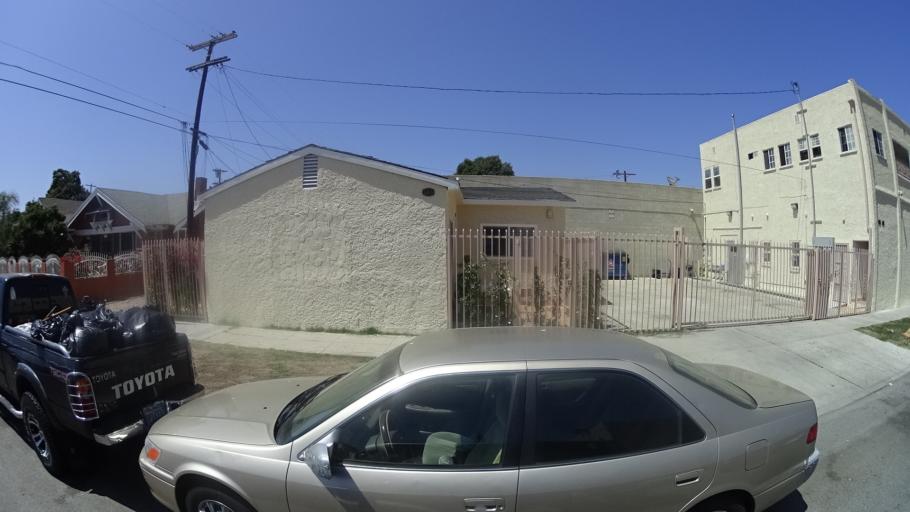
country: US
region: California
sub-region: Los Angeles County
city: View Park-Windsor Hills
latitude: 34.0029
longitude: -118.3005
